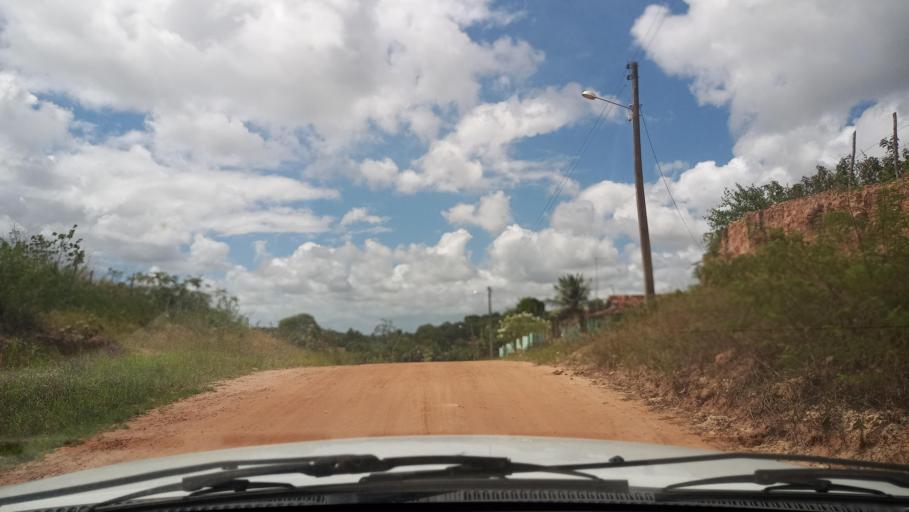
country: BR
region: Rio Grande do Norte
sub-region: Goianinha
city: Goianinha
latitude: -6.2622
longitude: -35.2623
